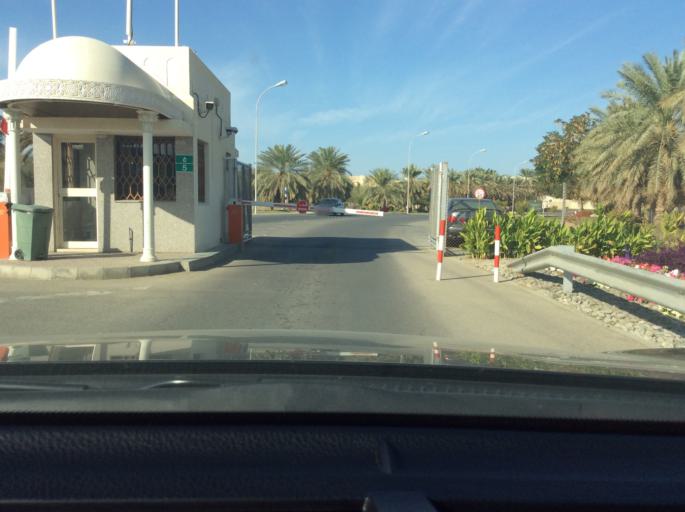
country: OM
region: Muhafazat Masqat
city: As Sib al Jadidah
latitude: 23.5825
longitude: 58.1705
